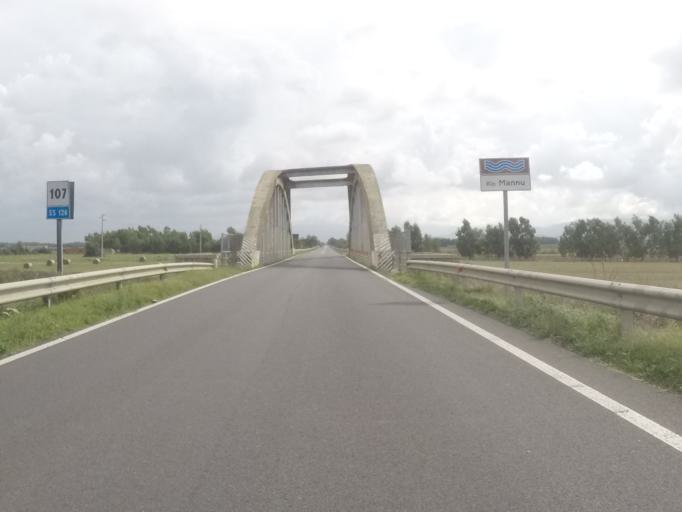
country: IT
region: Sardinia
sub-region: Provincia di Oristano
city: San Nicolo d'Arcidano
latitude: 39.6758
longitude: 8.6514
